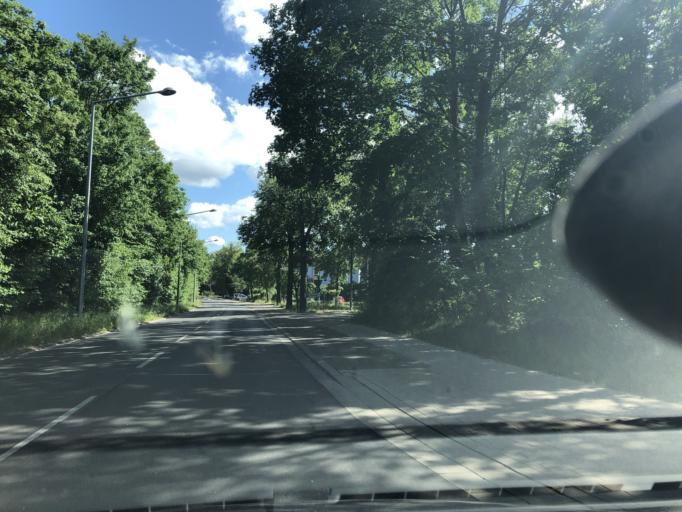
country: DE
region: Rheinland-Pfalz
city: Germersheim
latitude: 49.2171
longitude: 8.3783
